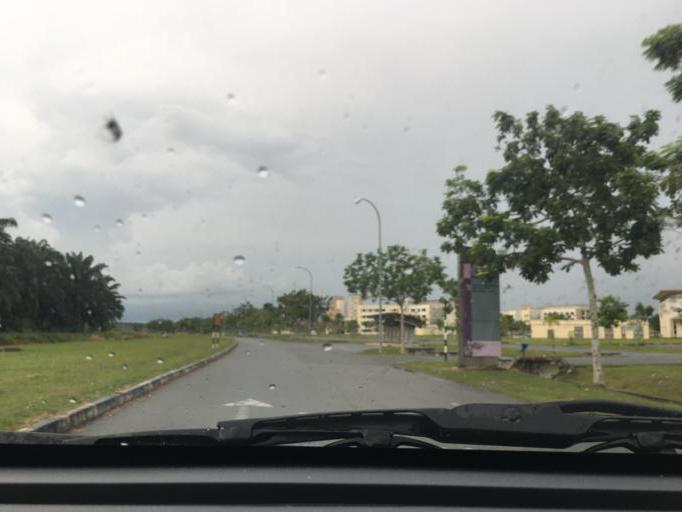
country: MY
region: Kedah
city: Sungai Petani
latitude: 5.5864
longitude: 100.6434
